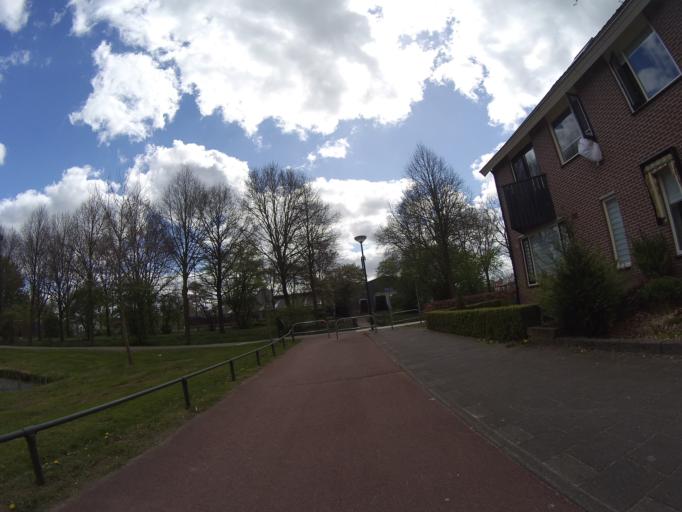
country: NL
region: Utrecht
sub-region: Gemeente Bunschoten
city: Spakenburg
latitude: 52.2352
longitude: 5.3633
